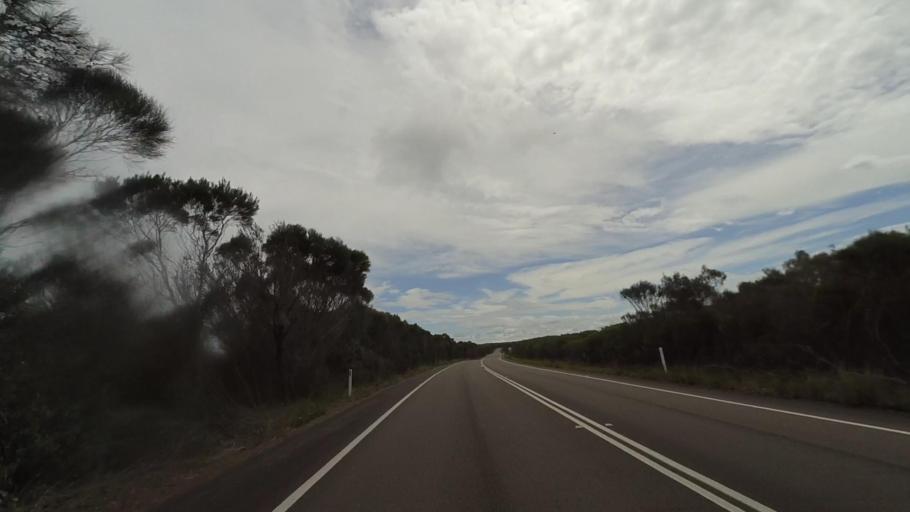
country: AU
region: New South Wales
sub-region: Sutherland Shire
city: Bundeena
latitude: -34.1023
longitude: 151.1189
